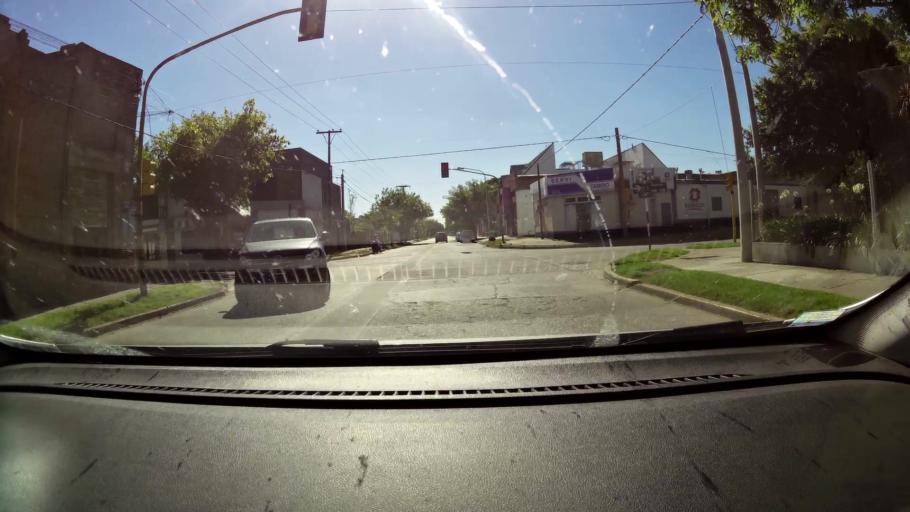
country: AR
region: Santa Fe
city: Rafaela
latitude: -31.2446
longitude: -61.4825
